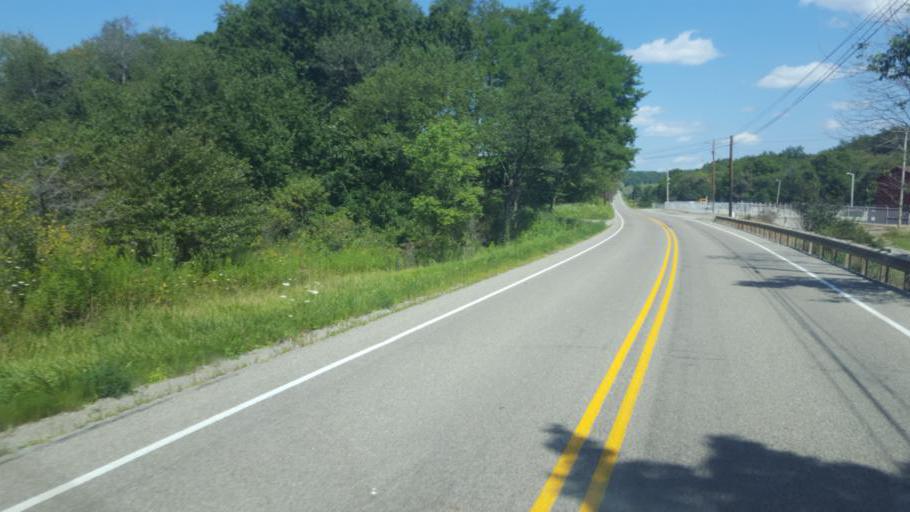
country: US
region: Pennsylvania
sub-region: Butler County
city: Chicora
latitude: 41.1009
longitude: -79.6579
